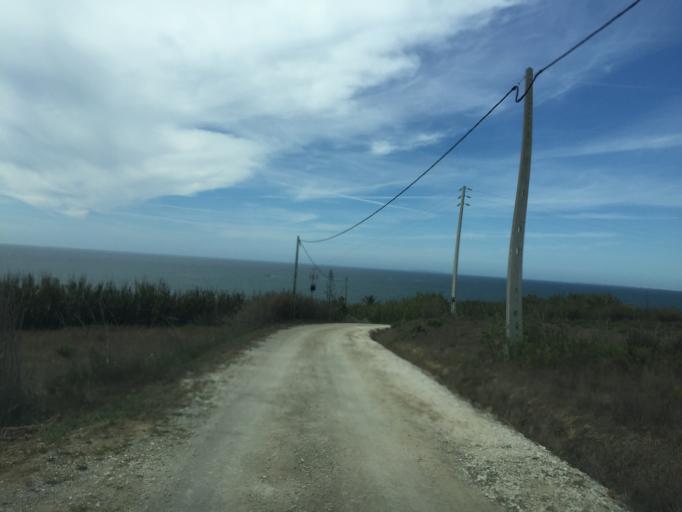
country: PT
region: Lisbon
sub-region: Lourinha
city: Lourinha
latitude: 39.1983
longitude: -9.3453
